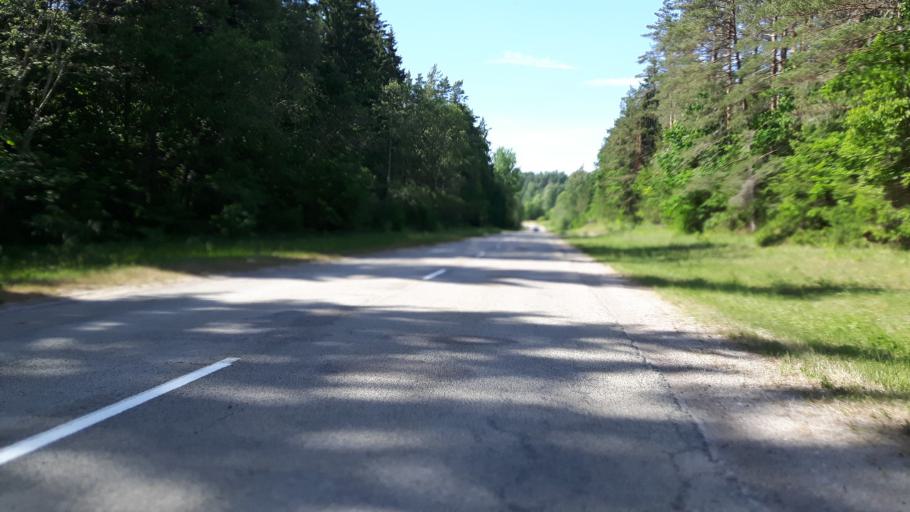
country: LV
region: Talsu Rajons
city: Sabile
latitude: 57.0811
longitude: 22.5276
